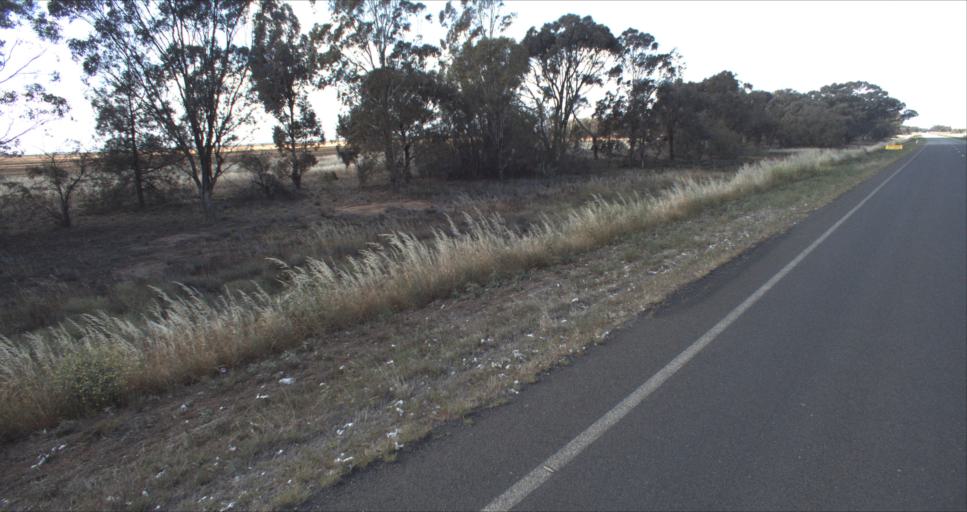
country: AU
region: New South Wales
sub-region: Murrumbidgee Shire
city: Darlington Point
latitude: -34.5428
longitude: 146.1718
